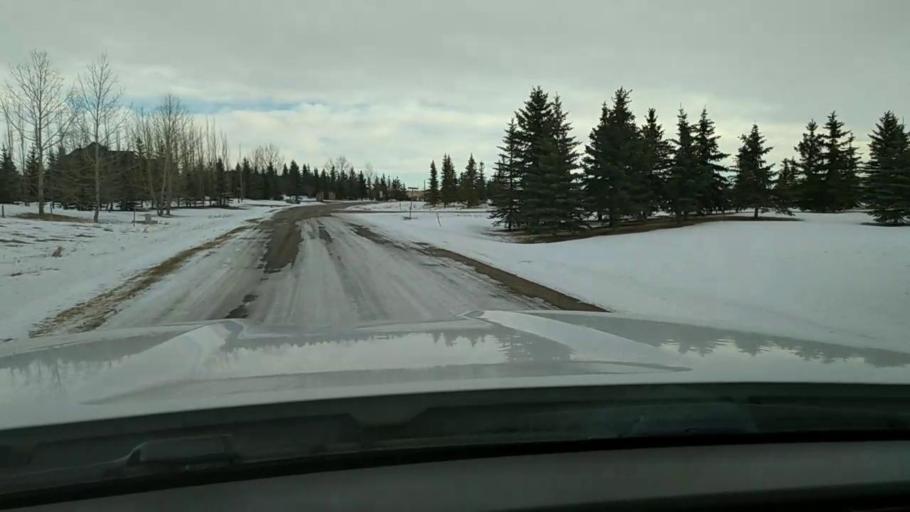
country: CA
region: Alberta
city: Cochrane
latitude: 51.2046
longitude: -114.2846
